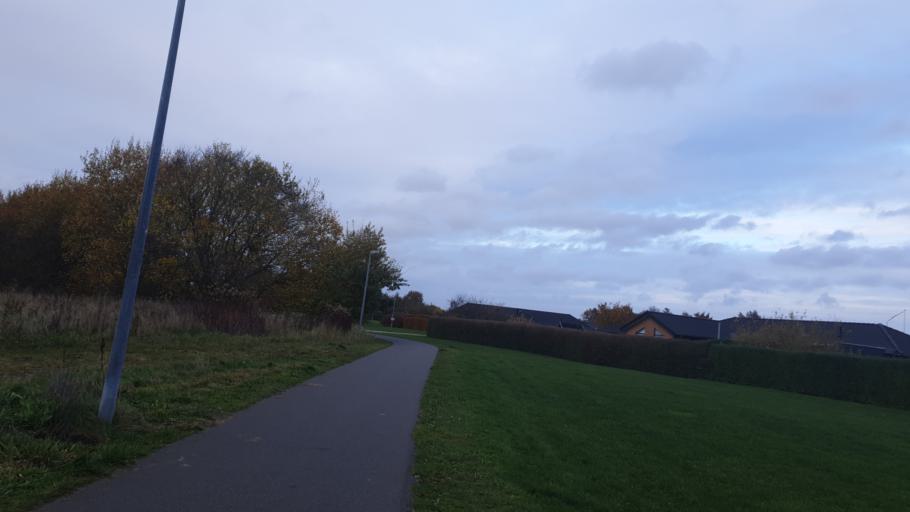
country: DK
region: Central Jutland
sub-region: Hedensted Kommune
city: Hedensted
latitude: 55.7877
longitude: 9.6921
